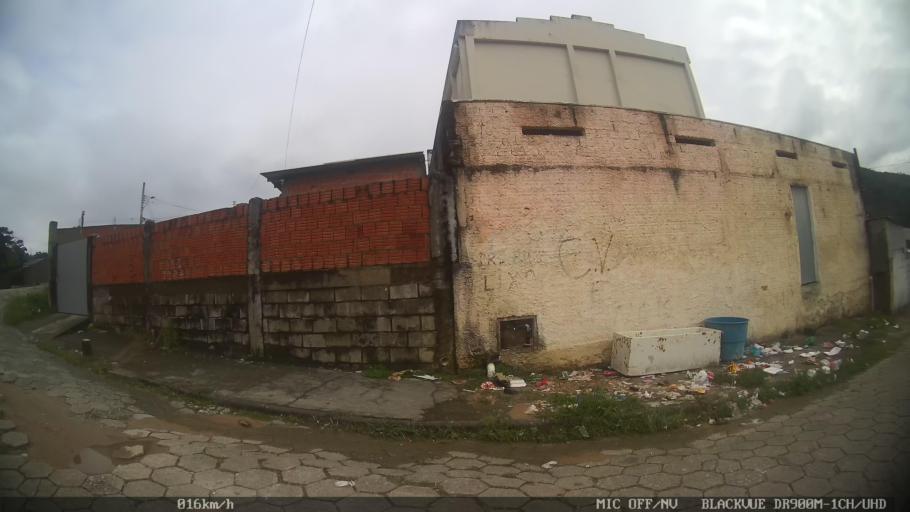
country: BR
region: Santa Catarina
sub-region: Biguacu
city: Biguacu
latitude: -27.5490
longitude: -48.6443
